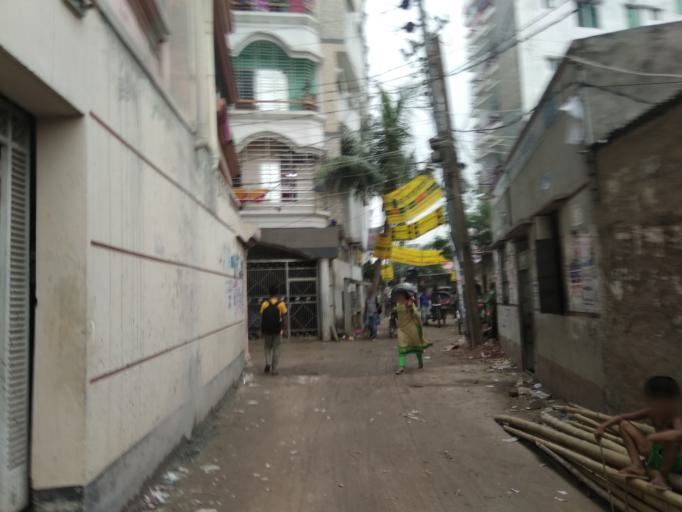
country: BD
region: Dhaka
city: Paltan
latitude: 23.7830
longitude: 90.4311
